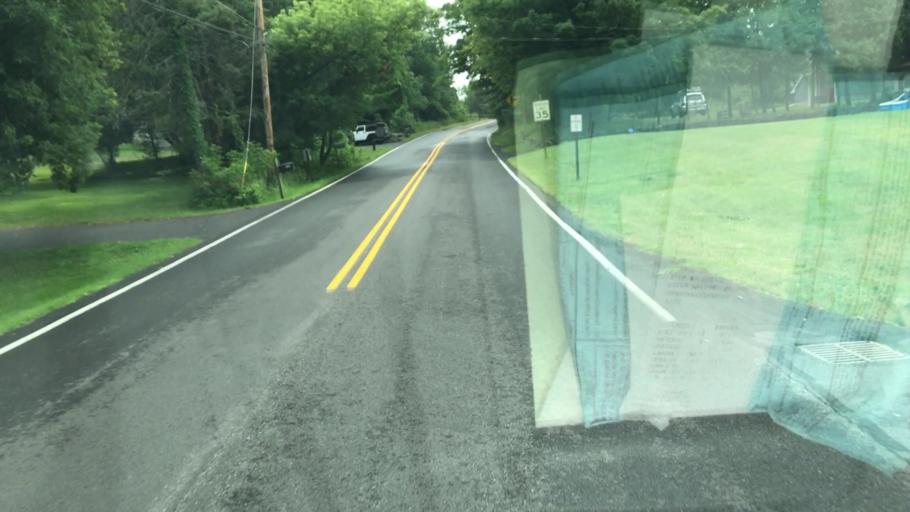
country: US
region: New York
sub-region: Onondaga County
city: Manlius
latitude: 42.9876
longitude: -75.9840
